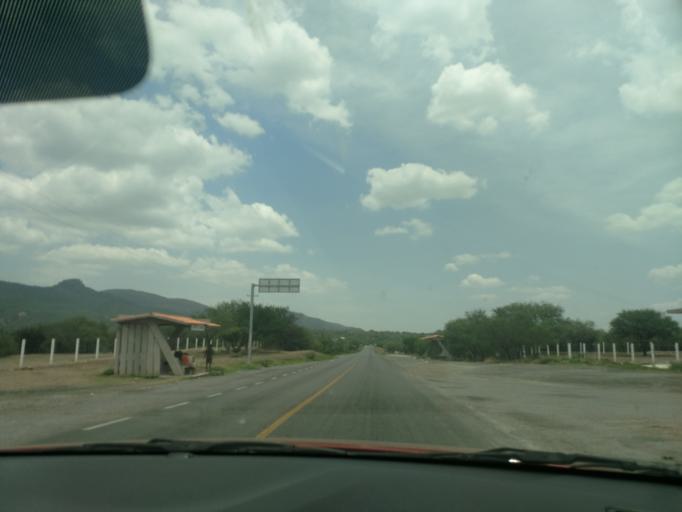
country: MX
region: San Luis Potosi
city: Villa Juarez
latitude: 22.0187
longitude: -100.3862
